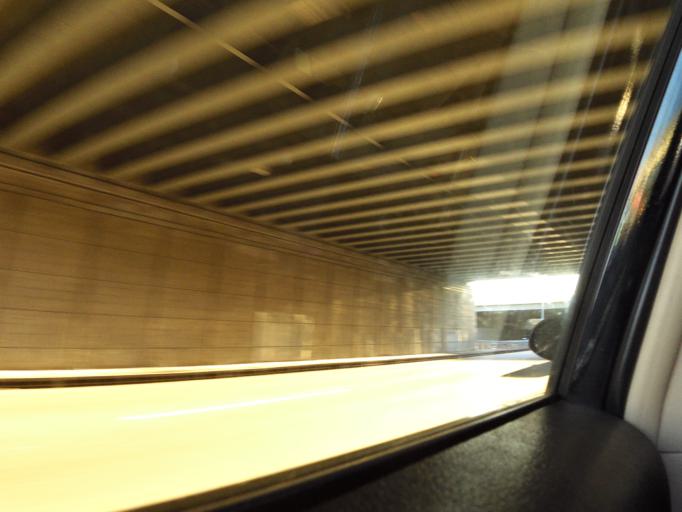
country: US
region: New York
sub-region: Queens County
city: Jamaica
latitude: 40.6448
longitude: -73.7947
